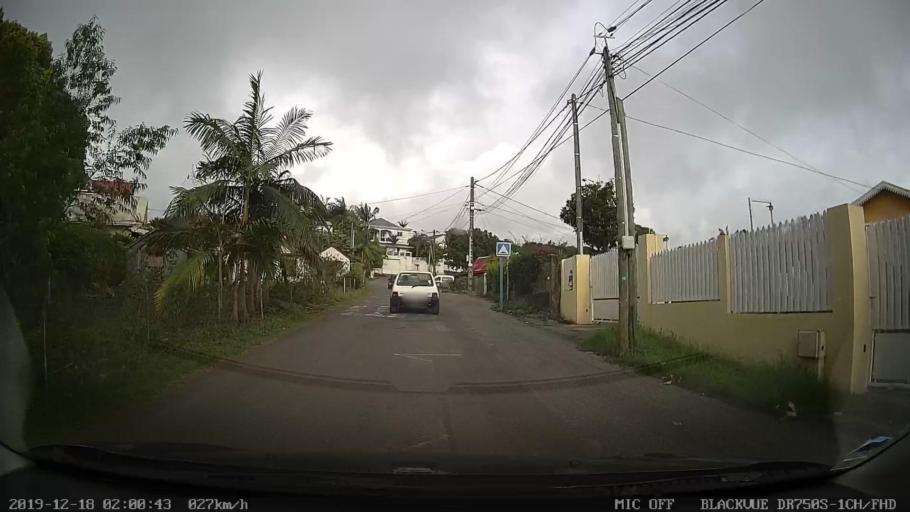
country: RE
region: Reunion
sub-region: Reunion
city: Le Tampon
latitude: -21.2526
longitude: 55.5186
